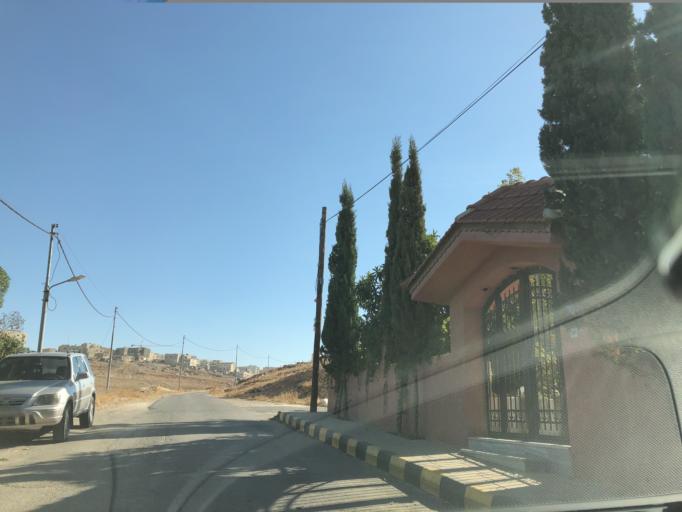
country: JO
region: Amman
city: Wadi as Sir
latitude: 31.9329
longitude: 35.8398
